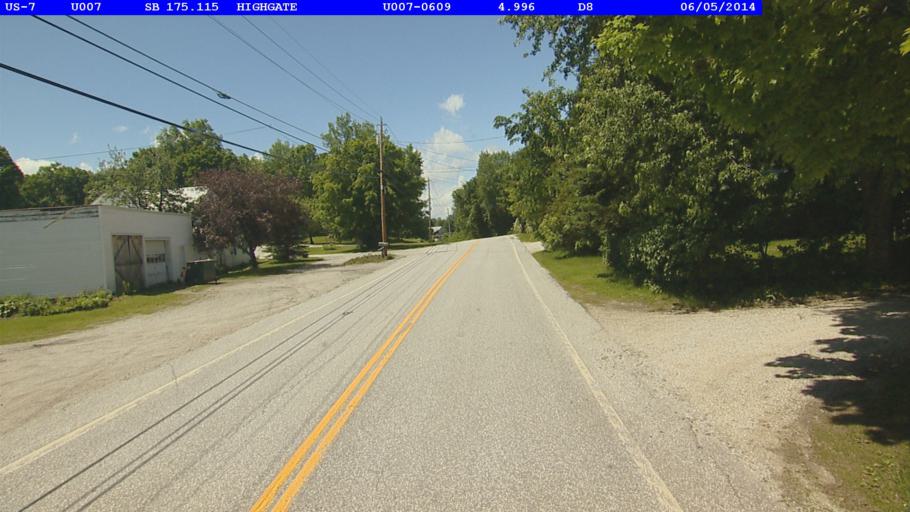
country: US
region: Vermont
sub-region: Franklin County
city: Swanton
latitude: 44.9973
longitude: -73.0800
